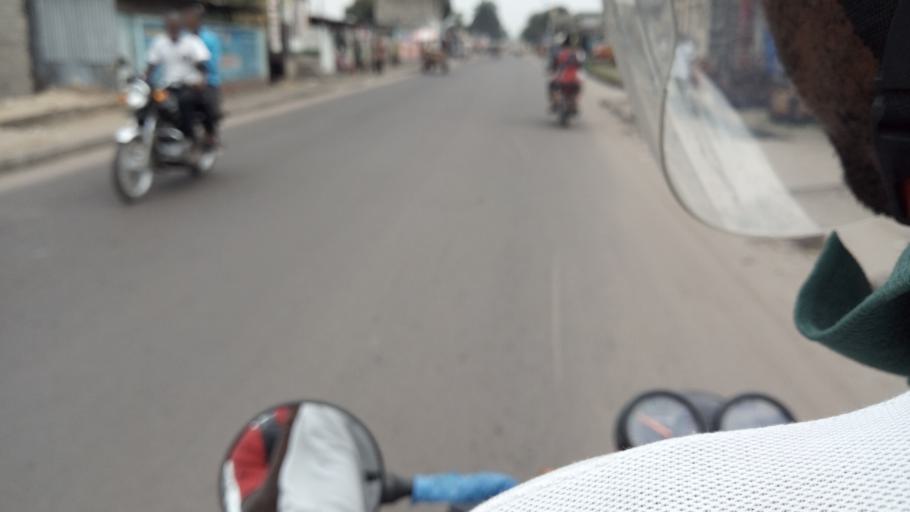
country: CD
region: Kinshasa
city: Masina
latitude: -4.4060
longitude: 15.3163
